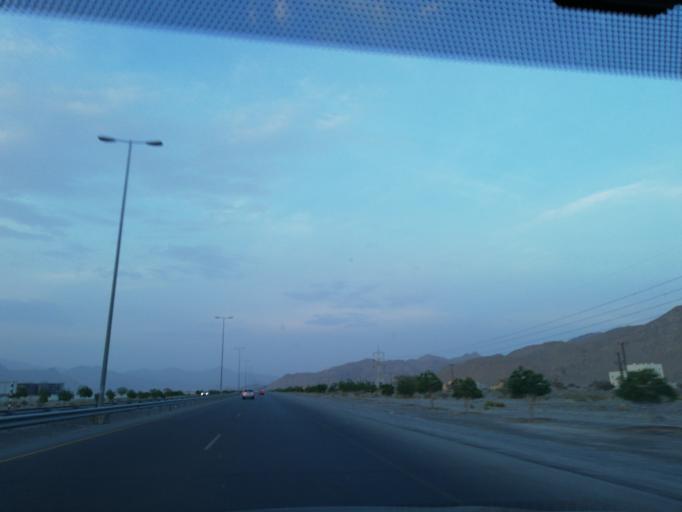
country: OM
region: Muhafazat ad Dakhiliyah
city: Nizwa
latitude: 22.8654
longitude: 57.5991
